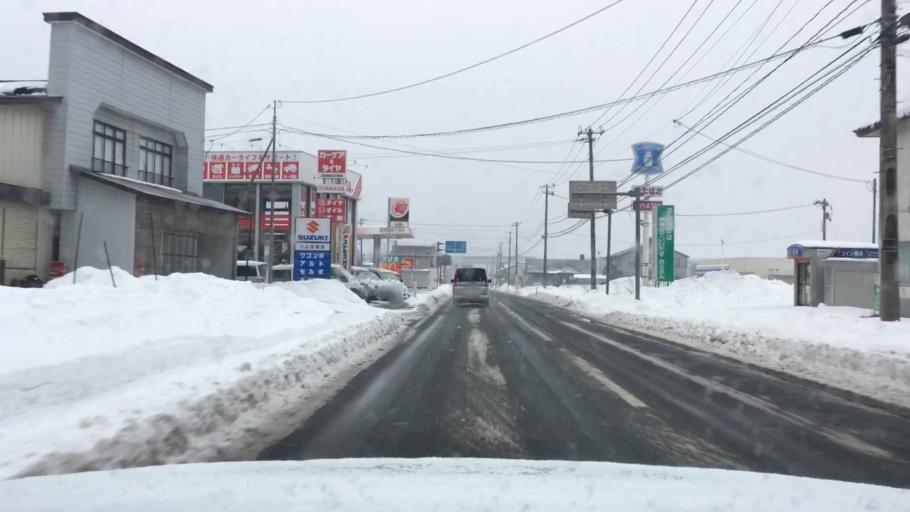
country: JP
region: Iwate
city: Ichinohe
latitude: 40.1060
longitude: 141.0502
